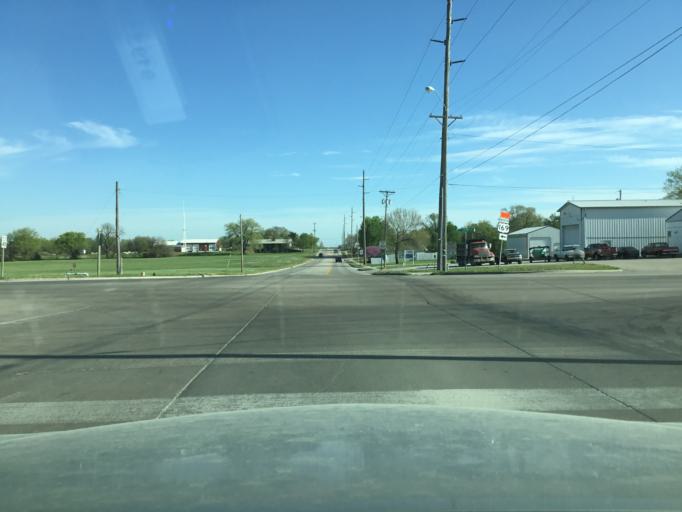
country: US
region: Kansas
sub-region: Neosho County
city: Chanute
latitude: 37.6888
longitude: -95.4711
